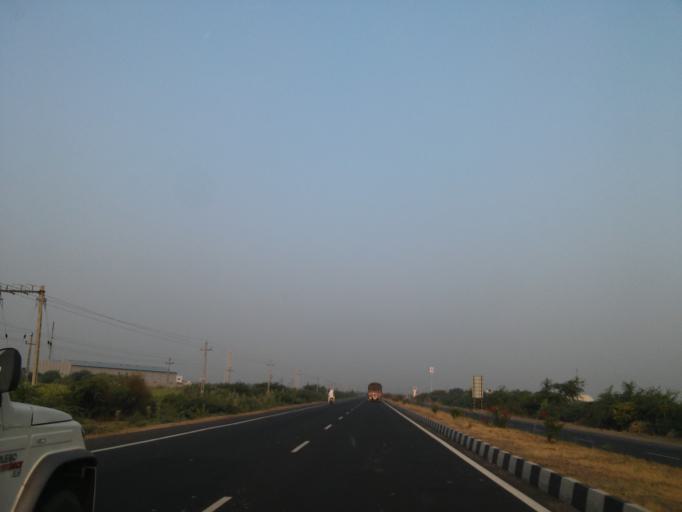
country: IN
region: Gujarat
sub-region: Kachchh
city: Bhachau
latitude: 23.2729
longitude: 70.6150
